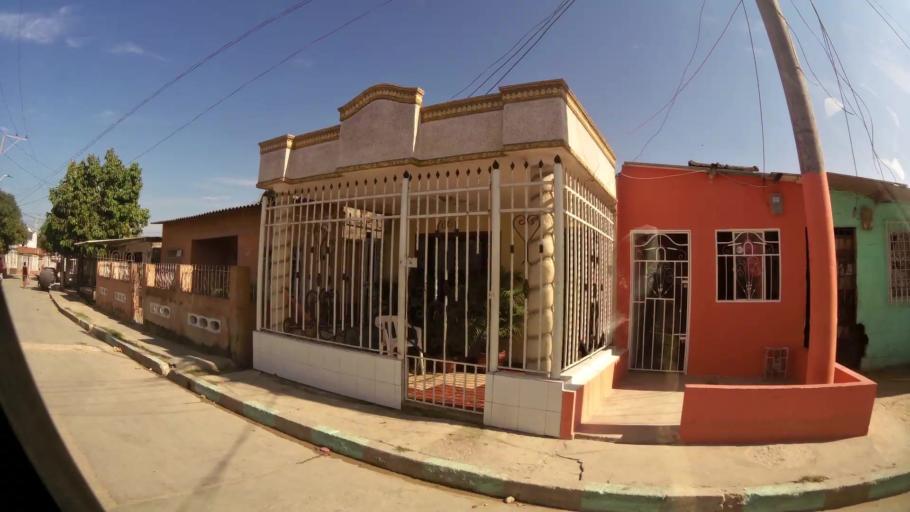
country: CO
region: Atlantico
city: Soledad
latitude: 10.9282
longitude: -74.8148
